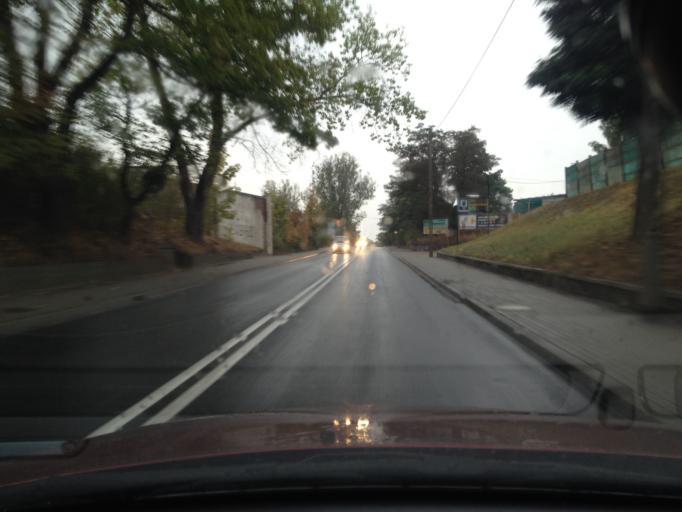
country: PL
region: Lubusz
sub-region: Powiat zaganski
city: Zagan
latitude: 51.6112
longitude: 15.3034
